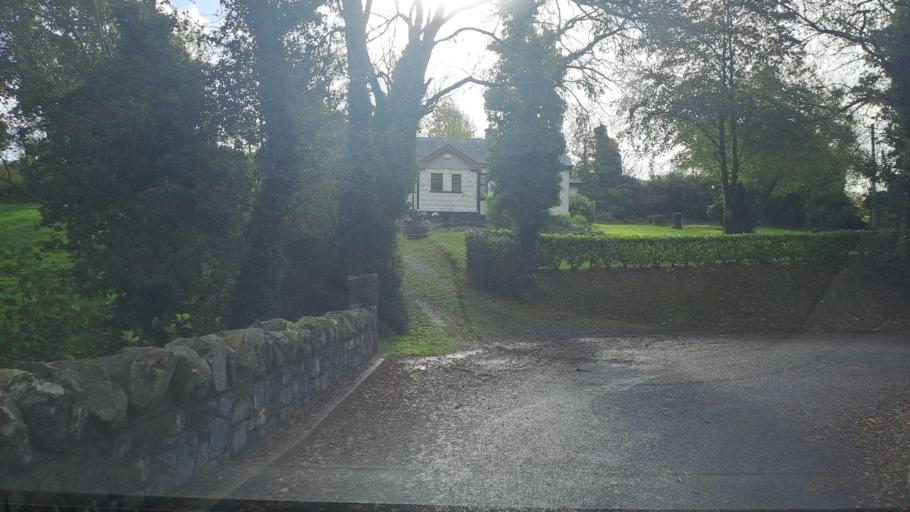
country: IE
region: Ulster
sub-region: An Cabhan
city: Cootehill
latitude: 54.0382
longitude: -6.9971
